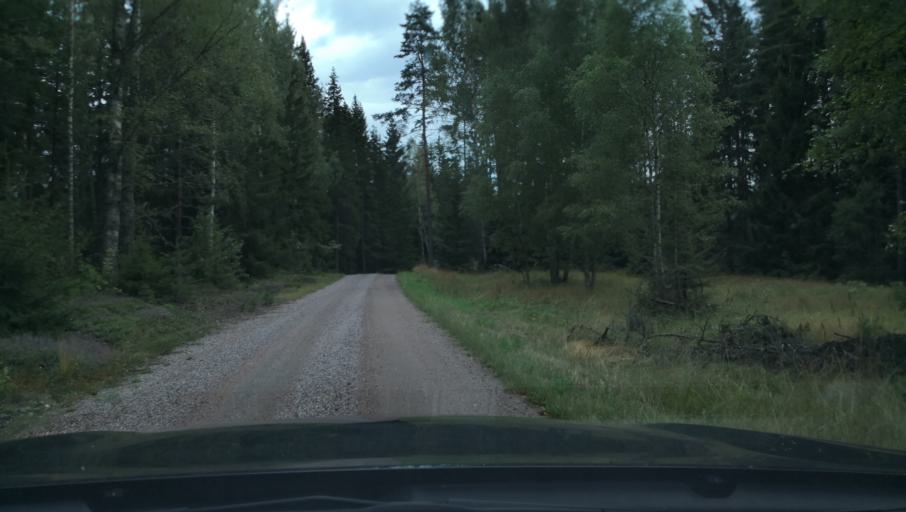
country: SE
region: Vaestmanland
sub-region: Arboga Kommun
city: Tyringe
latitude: 59.3558
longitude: 15.9985
